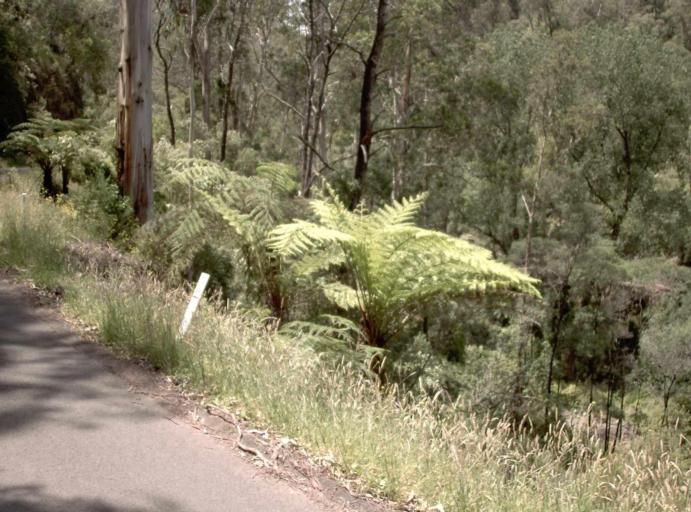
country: AU
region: Victoria
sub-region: Latrobe
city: Traralgon
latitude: -37.9533
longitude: 146.4257
